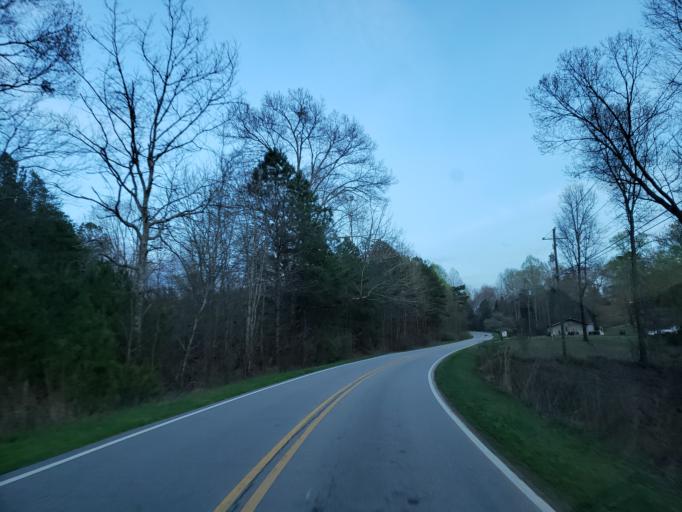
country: US
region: Georgia
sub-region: Polk County
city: Rockmart
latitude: 33.9905
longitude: -84.9572
